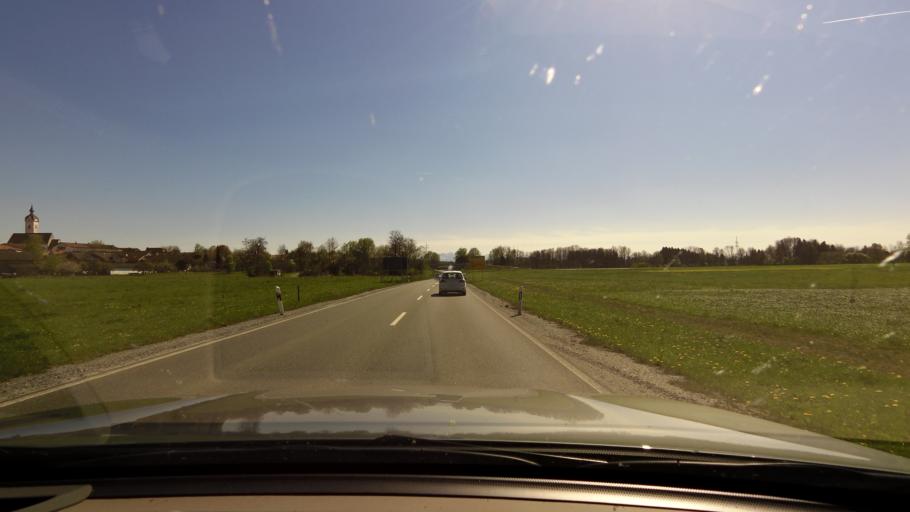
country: DE
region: Bavaria
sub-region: Upper Bavaria
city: Vogtareuth
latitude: 47.9521
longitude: 12.1798
